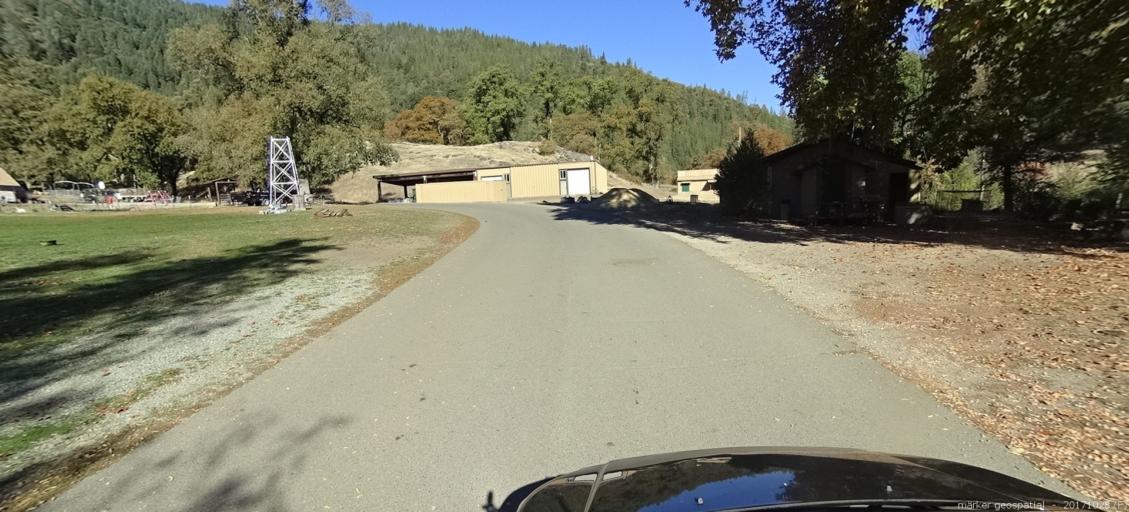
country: US
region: California
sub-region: Trinity County
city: Lewiston
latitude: 40.7887
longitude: -122.6102
